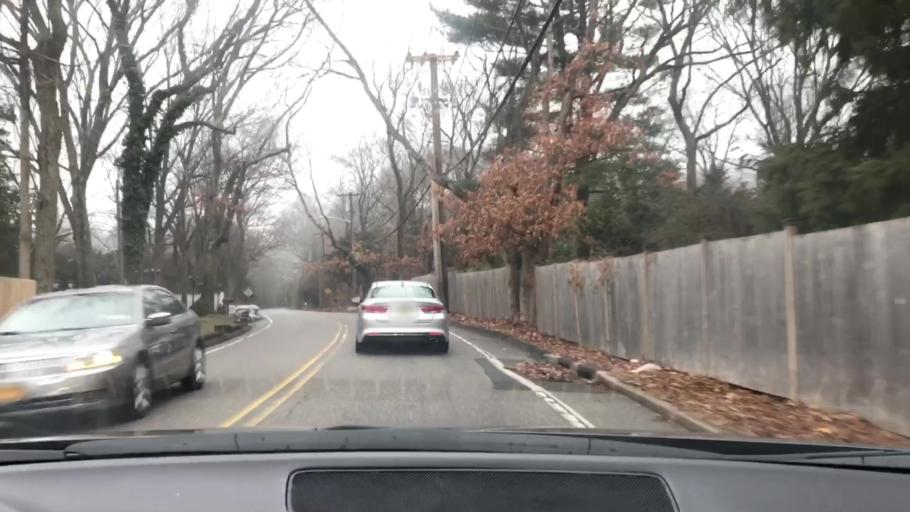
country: US
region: New York
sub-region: Suffolk County
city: South Huntington
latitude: 40.8235
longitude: -73.3719
